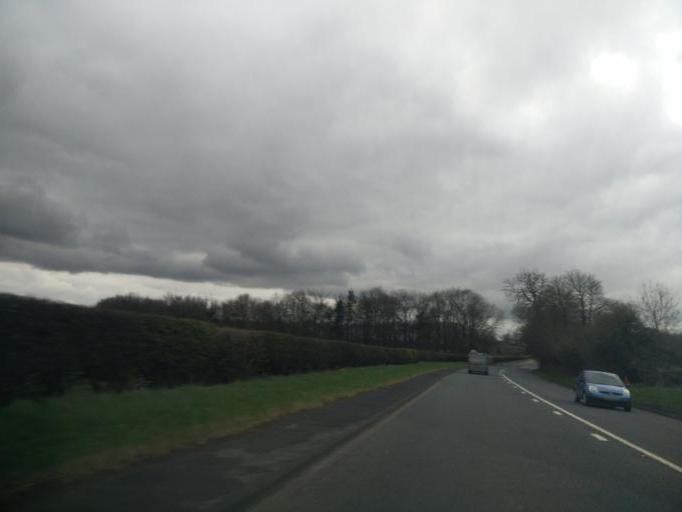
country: GB
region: England
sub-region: County Durham
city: Ushaw Moor
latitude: 54.7448
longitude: -1.6347
